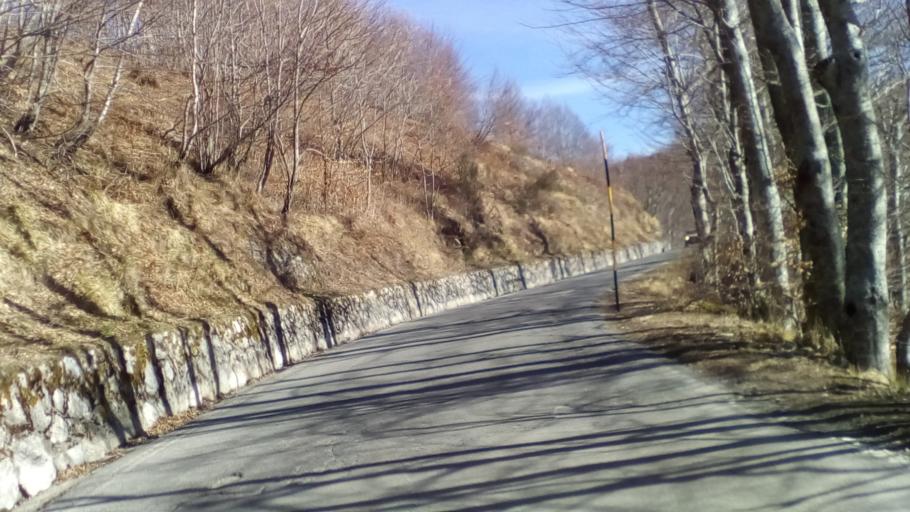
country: IT
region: Tuscany
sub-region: Provincia di Lucca
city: Castiglione di Garfagnana
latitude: 44.1801
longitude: 10.4682
